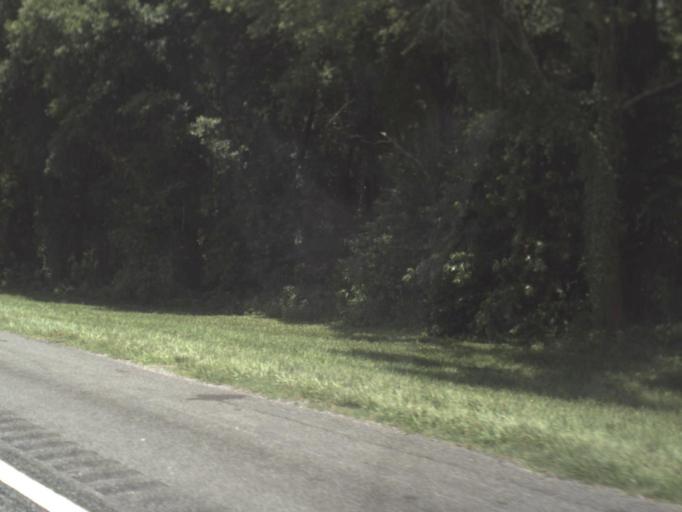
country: US
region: Florida
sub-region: Columbia County
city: Lake City
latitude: 30.1425
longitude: -82.6697
